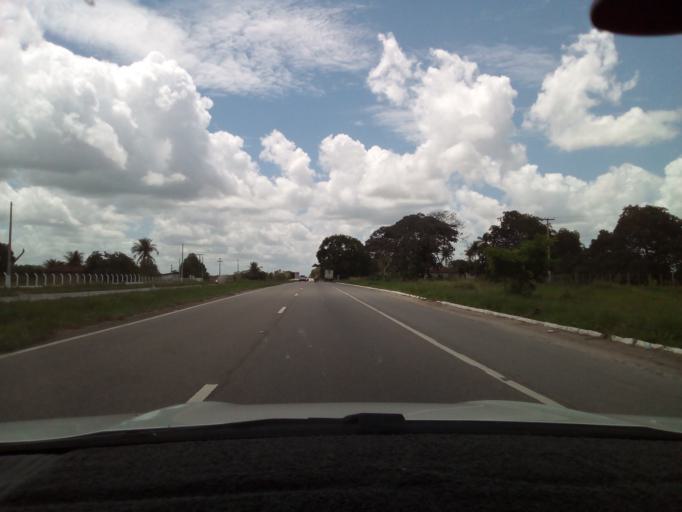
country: BR
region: Paraiba
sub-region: Pilar
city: Pilar
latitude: -7.1849
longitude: -35.2962
